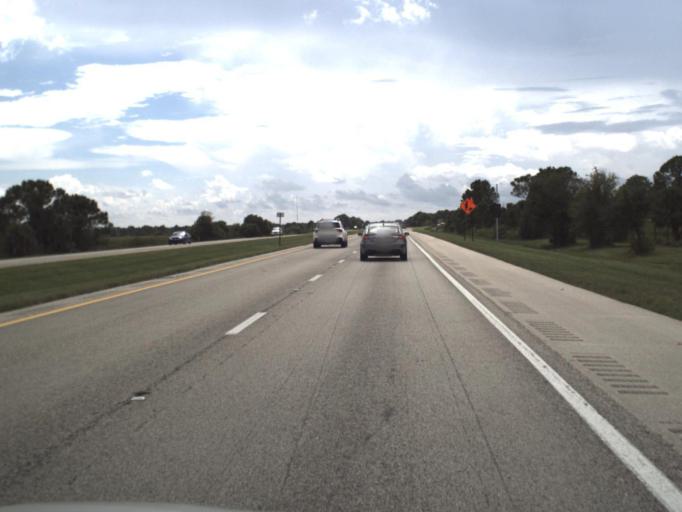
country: US
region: Florida
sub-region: Sarasota County
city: Laurel
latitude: 27.1865
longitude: -82.4421
